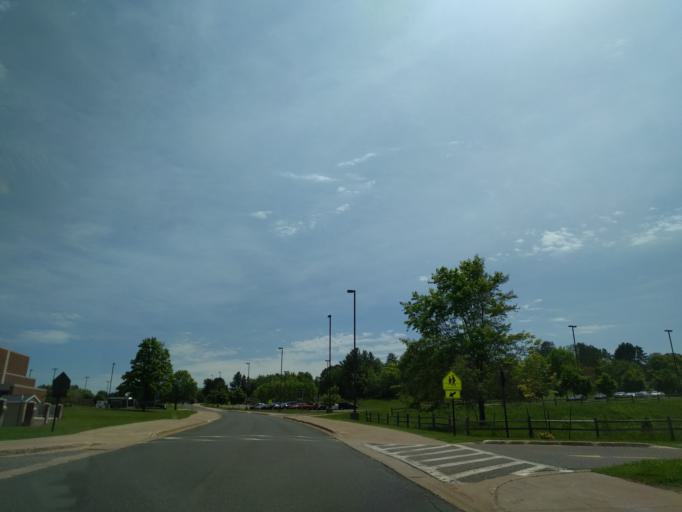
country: US
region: Michigan
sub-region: Marquette County
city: Marquette
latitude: 46.5590
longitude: -87.4094
